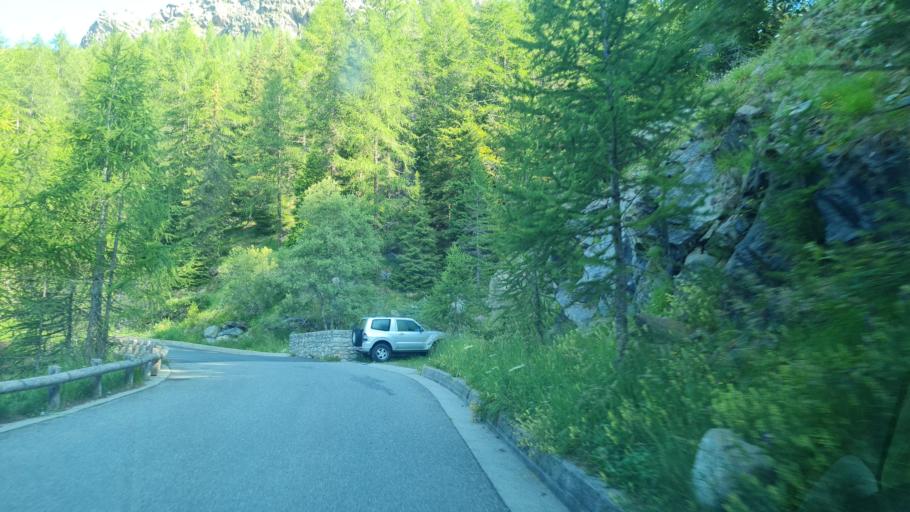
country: IT
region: Aosta Valley
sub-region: Valle d'Aosta
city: Champorcher
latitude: 45.6291
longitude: 7.6055
